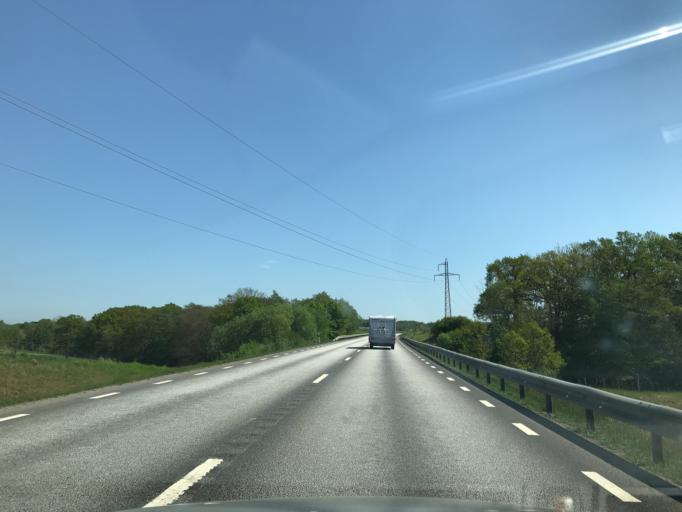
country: SE
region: Skane
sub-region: Klippans Kommun
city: Klippan
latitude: 56.1177
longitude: 13.1318
